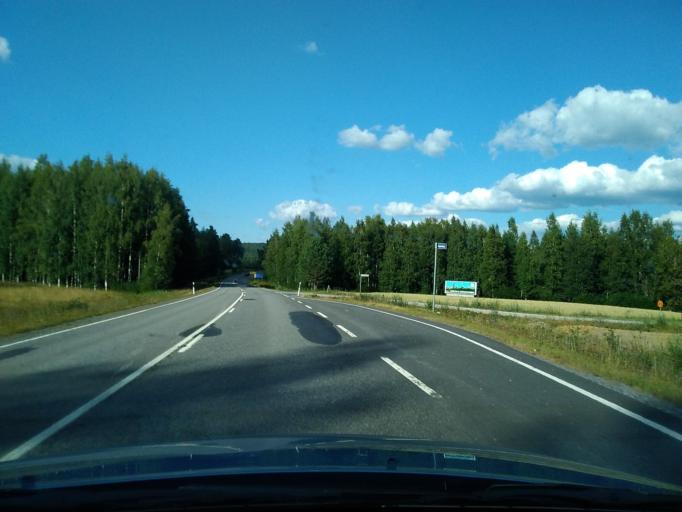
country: FI
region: Pirkanmaa
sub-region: Ylae-Pirkanmaa
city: Maenttae
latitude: 61.9918
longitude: 24.6356
